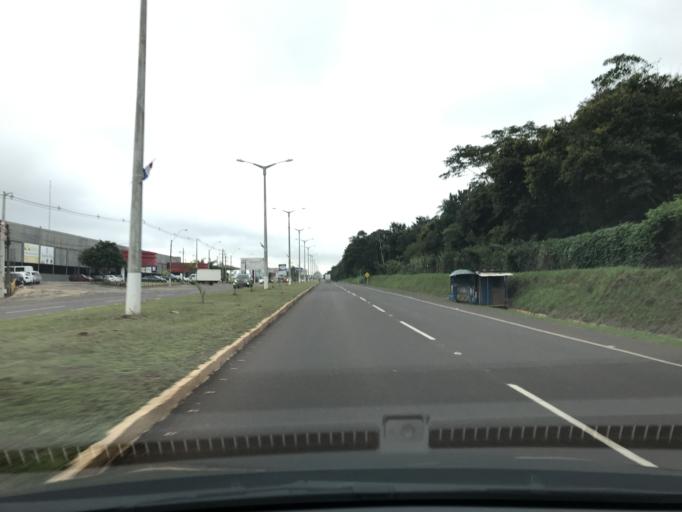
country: PY
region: Canindeyu
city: Salto del Guaira
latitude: -24.0175
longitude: -54.3254
